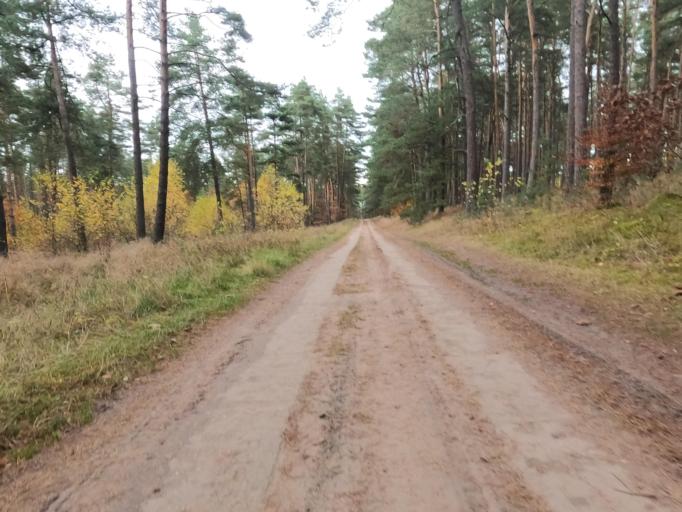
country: PL
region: Pomeranian Voivodeship
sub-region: Powiat starogardzki
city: Skarszewy
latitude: 54.0555
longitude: 18.4432
